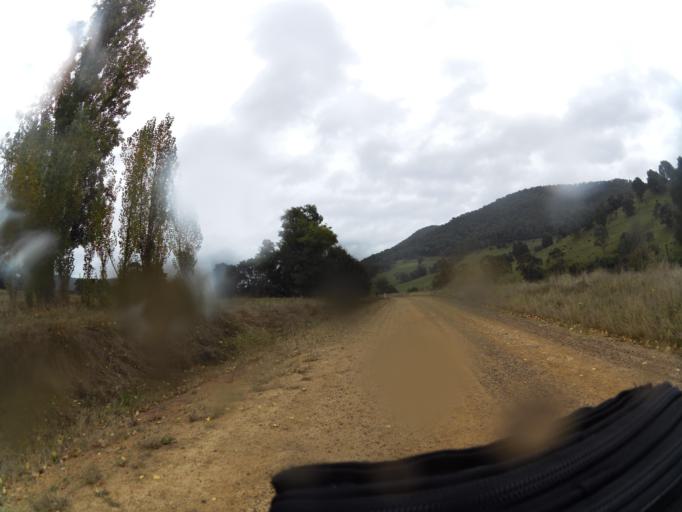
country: AU
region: New South Wales
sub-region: Greater Hume Shire
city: Holbrook
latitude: -36.2372
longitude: 147.6314
